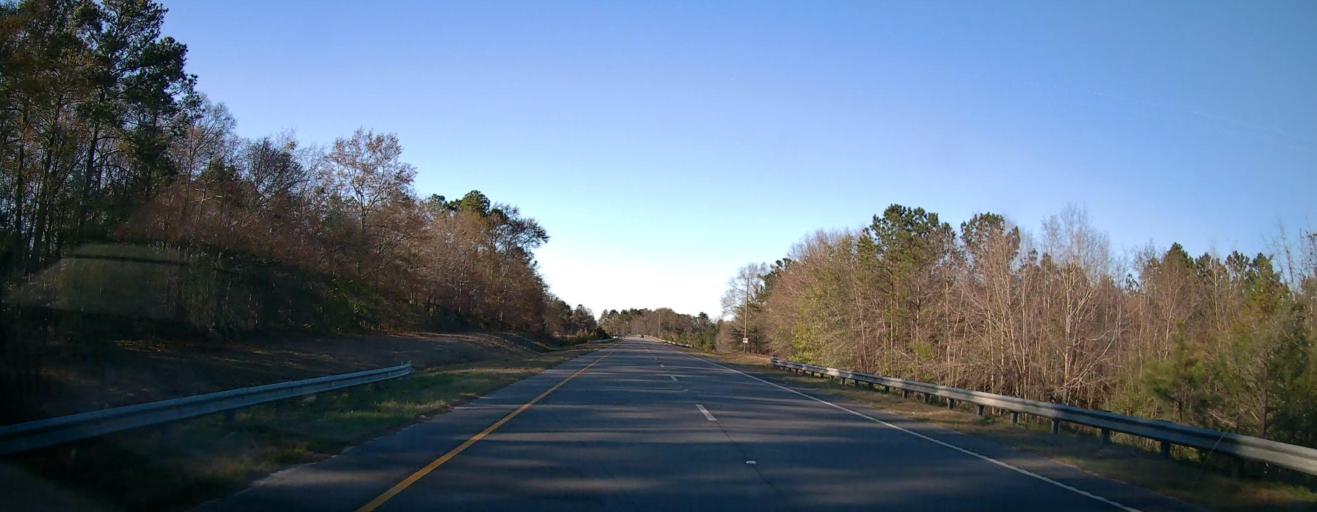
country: US
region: Georgia
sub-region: Taylor County
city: Butler
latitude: 32.5621
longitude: -84.2374
